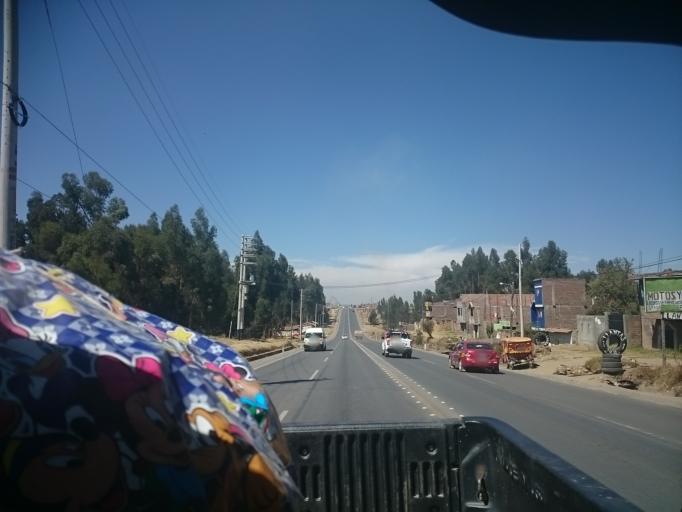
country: PE
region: Junin
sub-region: Provincia de Huancayo
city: San Agustin
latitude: -11.9695
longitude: -75.2696
